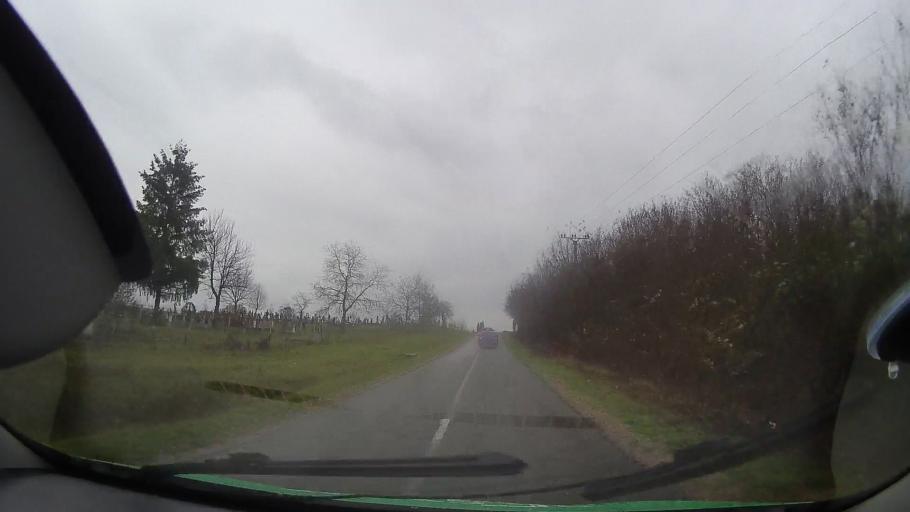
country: RO
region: Bihor
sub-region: Comuna Holod
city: Vintere
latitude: 46.7600
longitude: 22.1471
